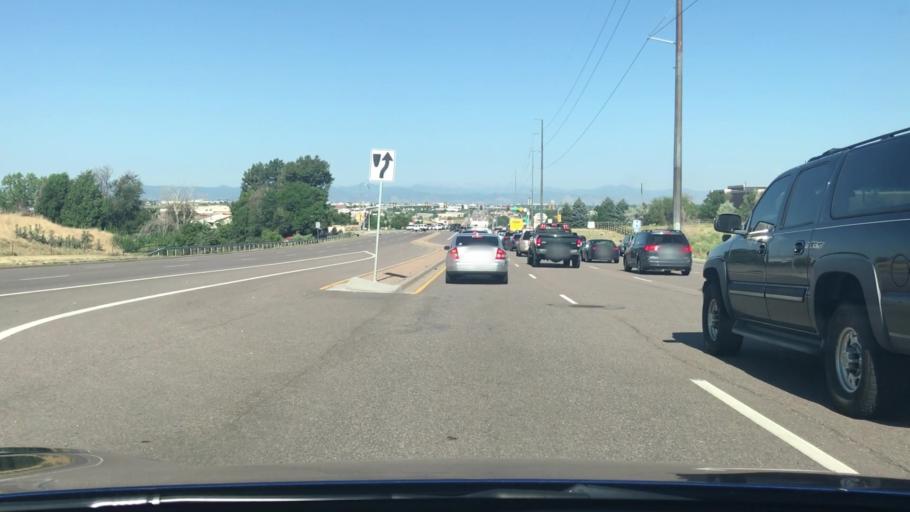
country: US
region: Colorado
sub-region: Arapahoe County
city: Dove Valley
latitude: 39.5950
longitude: -104.7942
